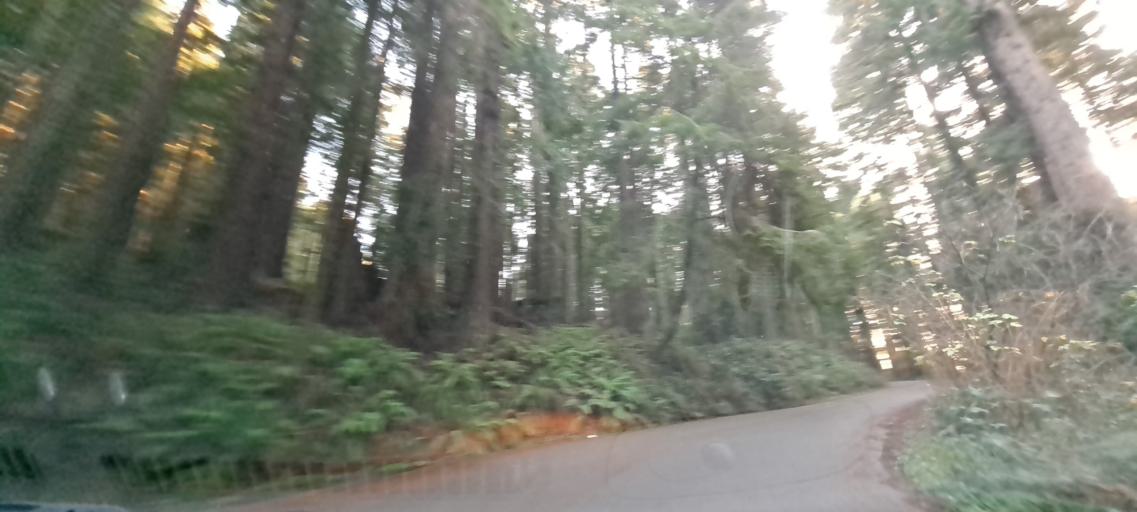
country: US
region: California
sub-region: Humboldt County
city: Arcata
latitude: 40.8711
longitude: -124.0726
